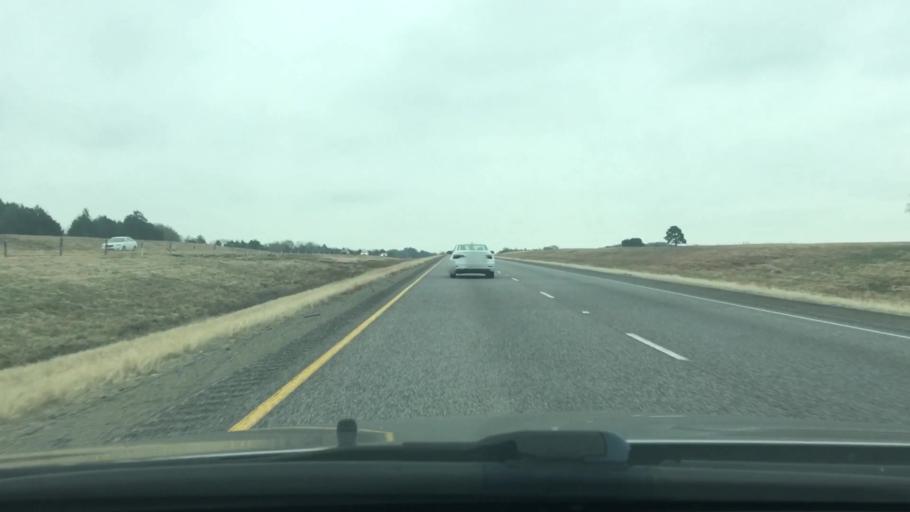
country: US
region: Texas
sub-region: Freestone County
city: Fairfield
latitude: 31.7855
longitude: -96.2401
